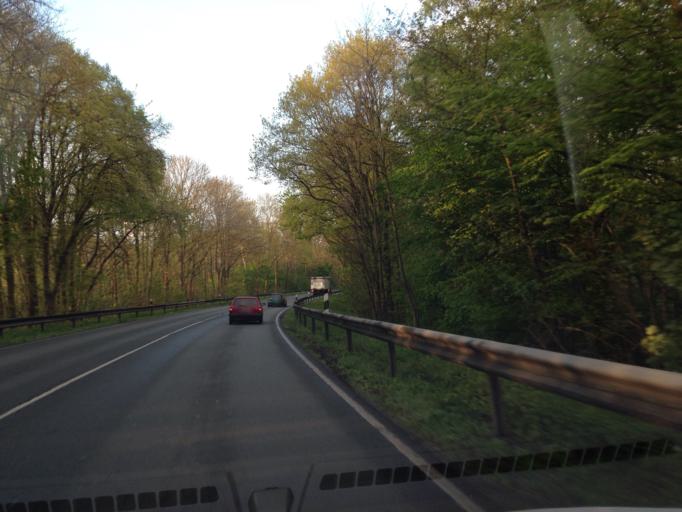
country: DE
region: North Rhine-Westphalia
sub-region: Regierungsbezirk Munster
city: Muenster
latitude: 51.9709
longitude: 7.6728
